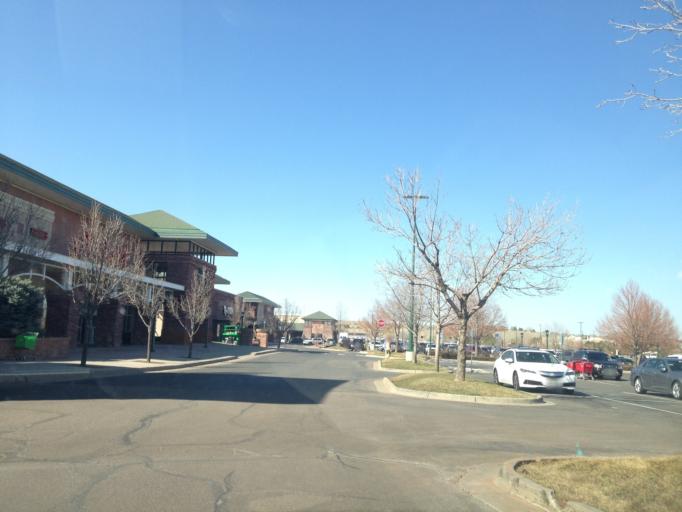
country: US
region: Colorado
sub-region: Boulder County
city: Superior
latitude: 39.9570
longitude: -105.1737
